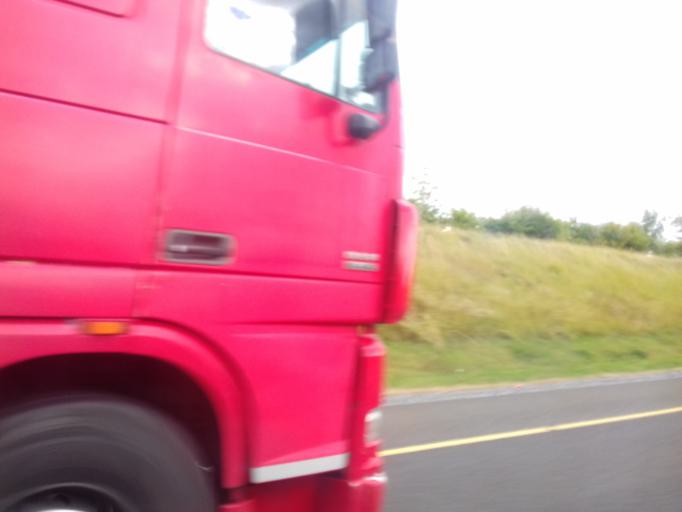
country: IE
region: Leinster
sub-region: Kilkenny
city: Thomastown
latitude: 52.6107
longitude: -7.1627
